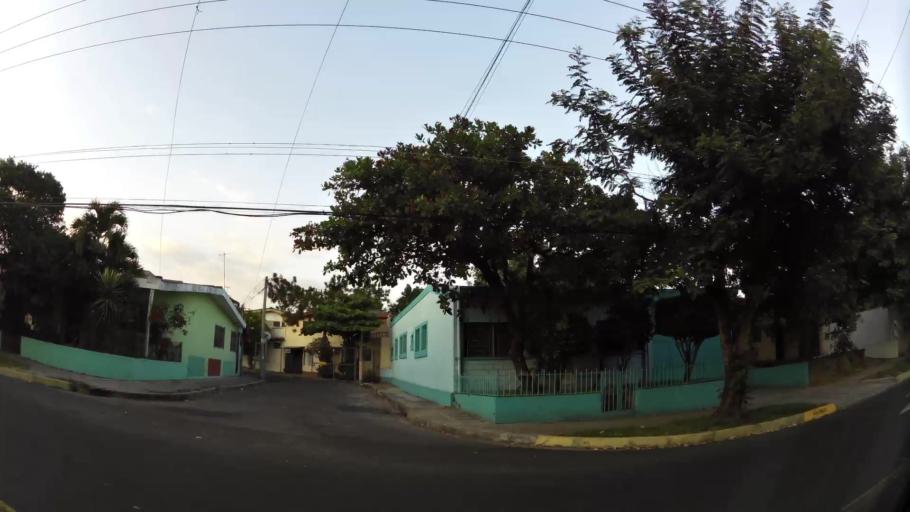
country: SV
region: San Salvador
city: Delgado
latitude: 13.7168
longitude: -89.1856
